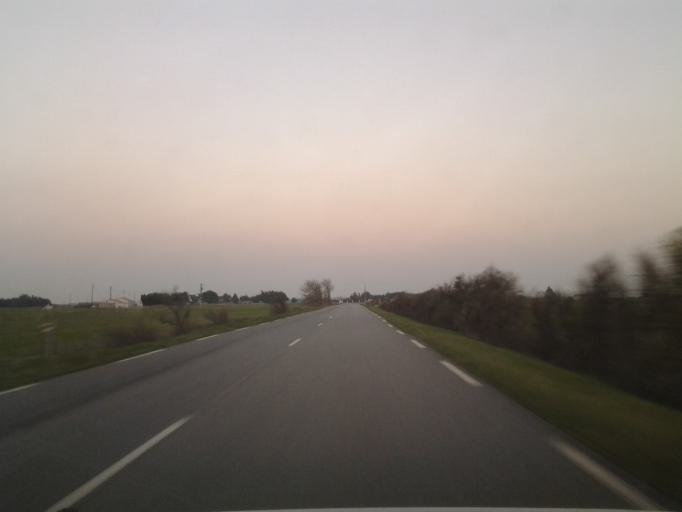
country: FR
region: Pays de la Loire
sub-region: Departement de la Vendee
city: Beauvoir-sur-Mer
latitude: 46.9211
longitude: -2.0893
